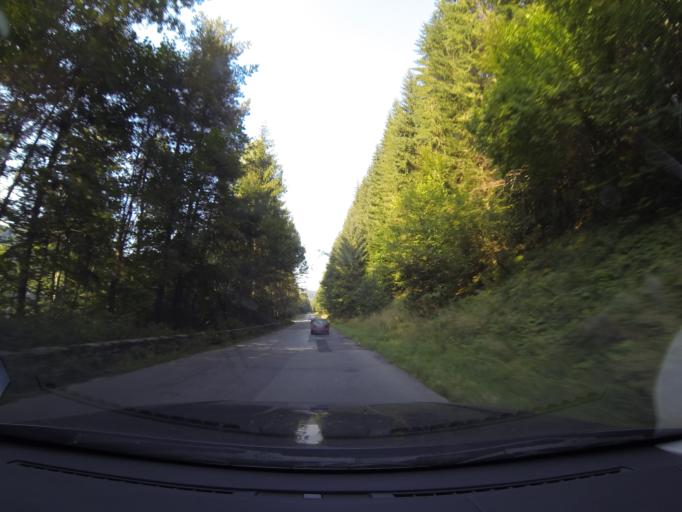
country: RO
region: Arges
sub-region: Comuna Arefu
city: Arefu
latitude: 45.3940
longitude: 24.6326
